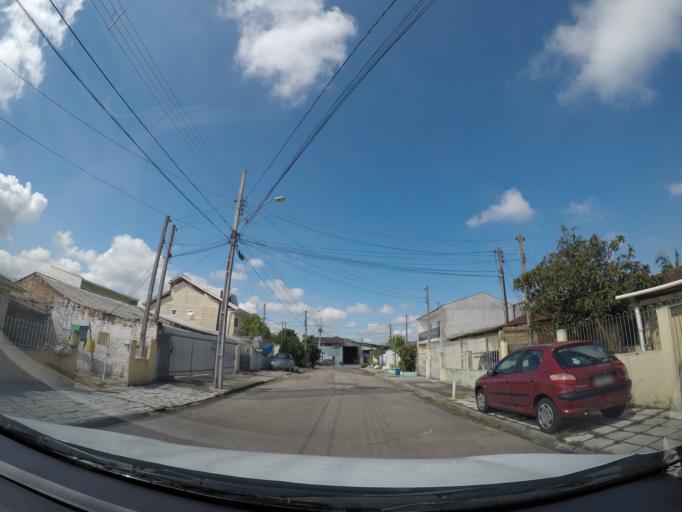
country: BR
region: Parana
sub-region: Sao Jose Dos Pinhais
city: Sao Jose dos Pinhais
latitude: -25.5022
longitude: -49.2179
